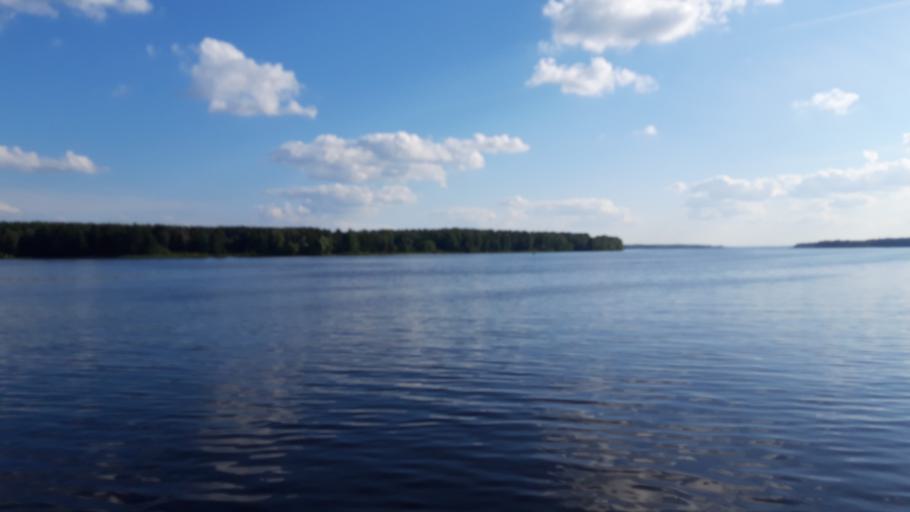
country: RU
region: Tverskaya
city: Konakovo
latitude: 56.7001
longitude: 36.7097
